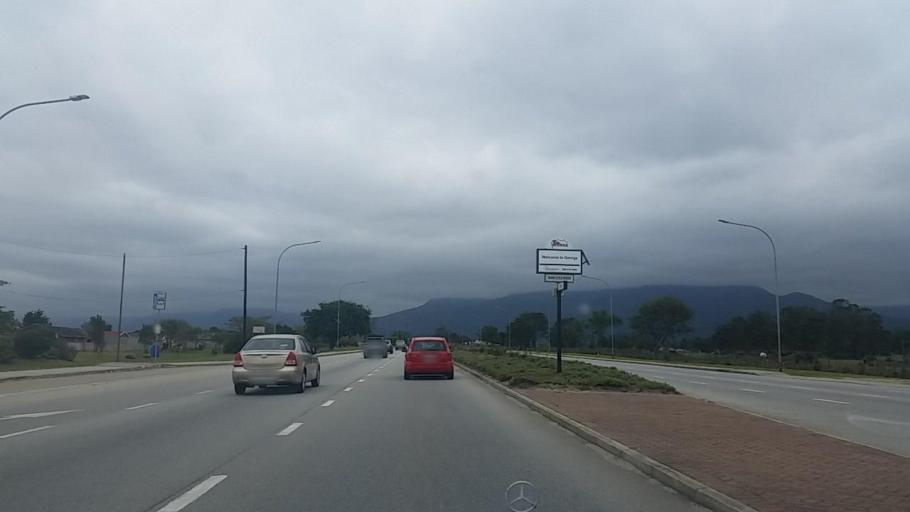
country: ZA
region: Western Cape
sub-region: Eden District Municipality
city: George
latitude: -33.9768
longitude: 22.4946
